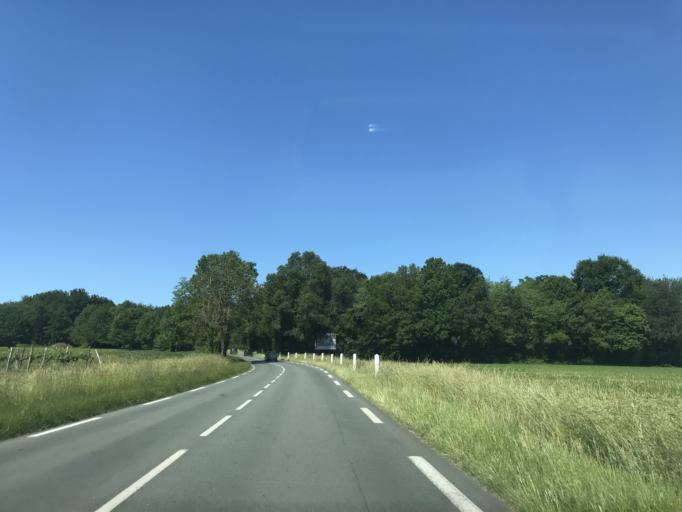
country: FR
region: Poitou-Charentes
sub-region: Departement de la Charente-Maritime
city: Cozes
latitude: 45.5794
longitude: -0.7984
